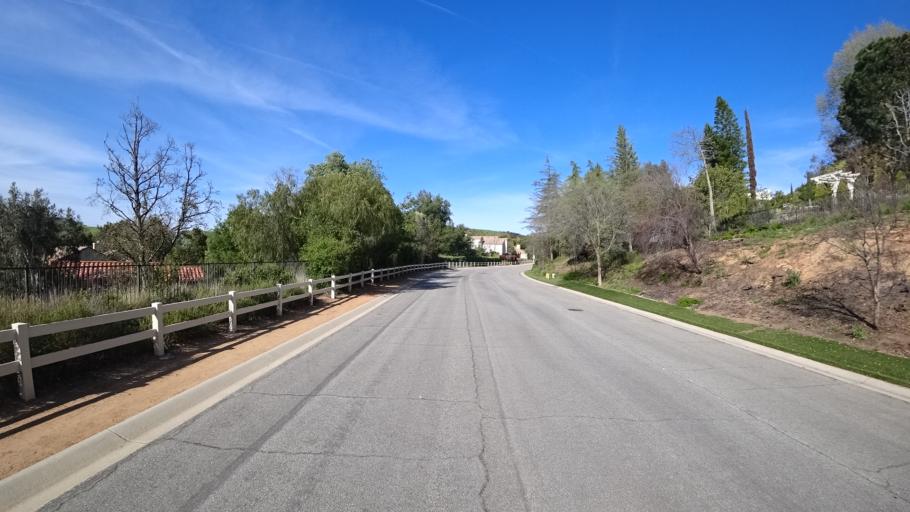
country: US
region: California
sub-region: Ventura County
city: Oak Park
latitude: 34.1962
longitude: -118.7913
